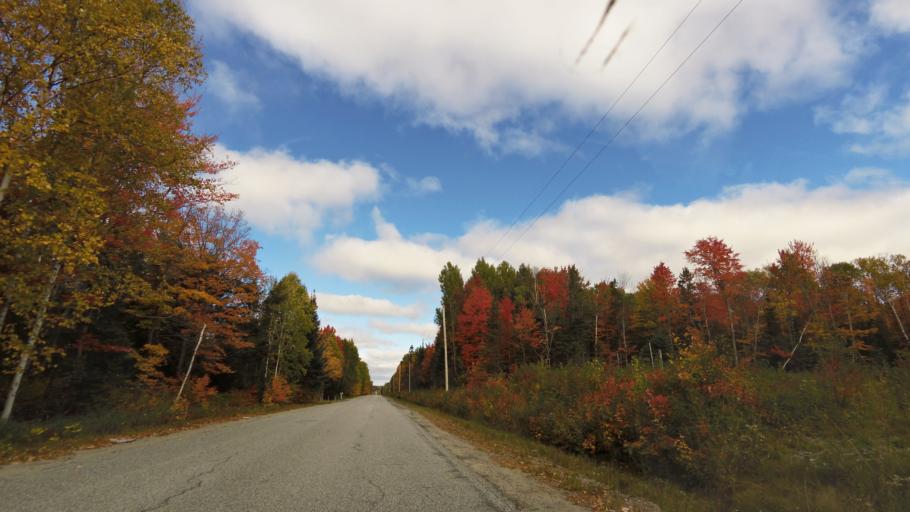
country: CA
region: Ontario
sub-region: Nipissing District
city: North Bay
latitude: 46.3551
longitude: -79.4871
